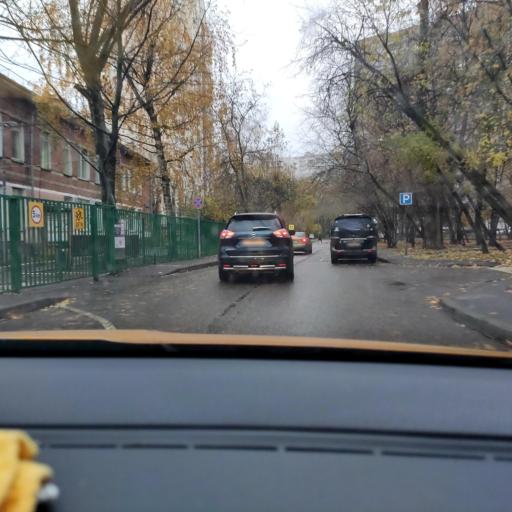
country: RU
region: Moscow
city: Ostankinskiy
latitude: 55.8160
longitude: 37.6263
